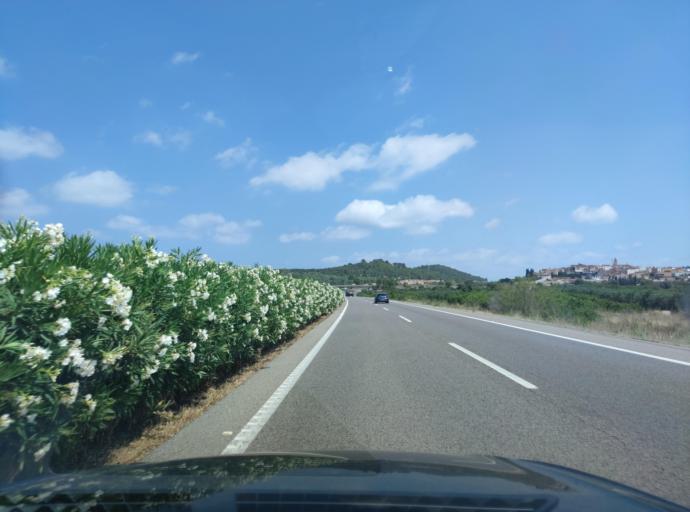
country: ES
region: Catalonia
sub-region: Provincia de Tarragona
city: Masdenverge
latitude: 40.6654
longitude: 0.5132
